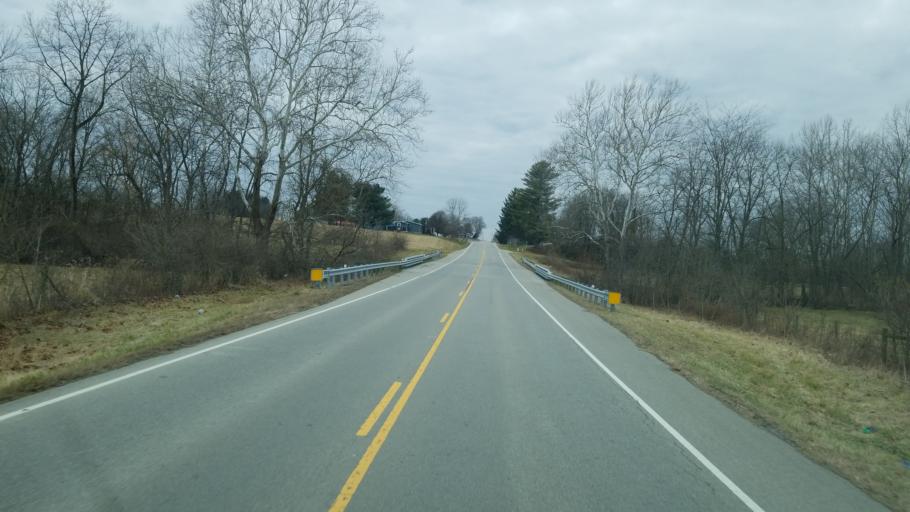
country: US
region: Ohio
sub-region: Highland County
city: Greenfield
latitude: 39.2188
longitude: -83.4300
